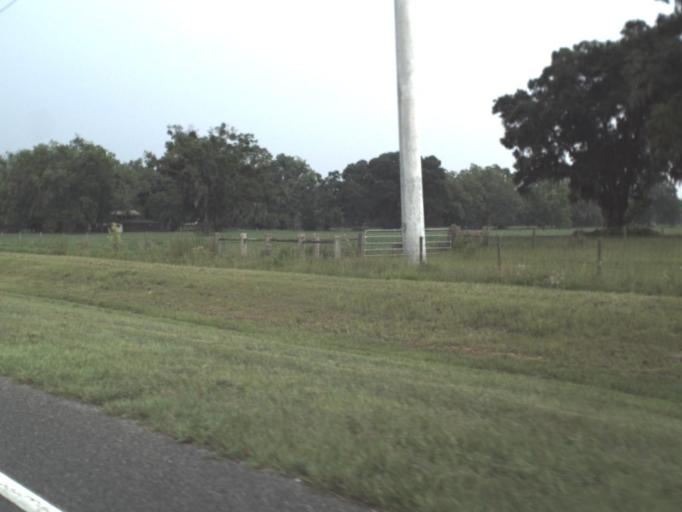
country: US
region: Florida
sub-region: Levy County
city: Chiefland
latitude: 29.4746
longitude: -82.8271
